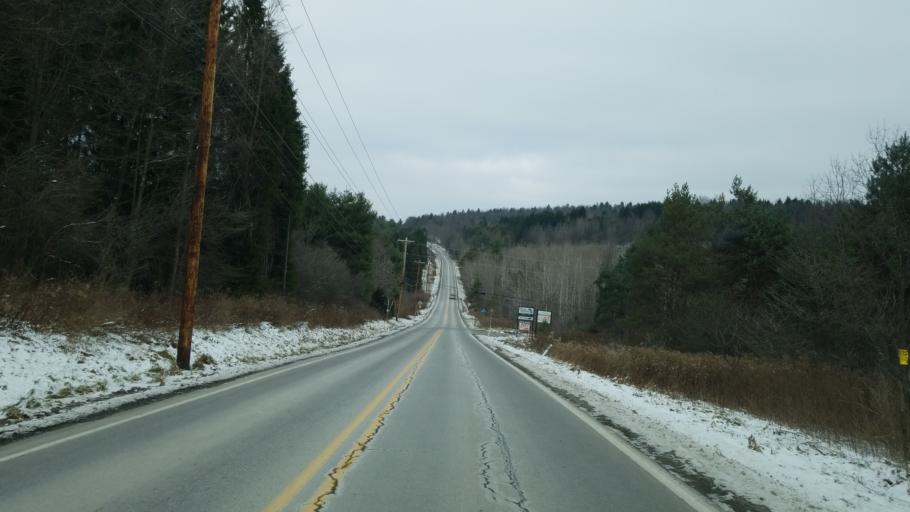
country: US
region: Pennsylvania
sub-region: Clearfield County
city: Sandy
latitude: 41.0760
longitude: -78.7350
